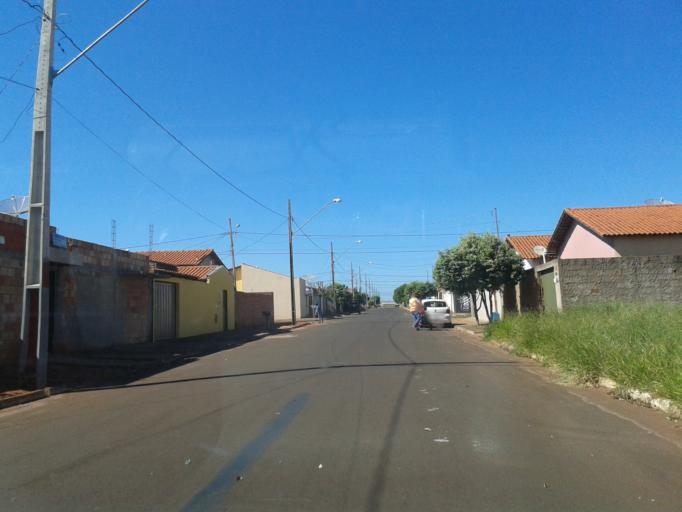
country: BR
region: Minas Gerais
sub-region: Santa Vitoria
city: Santa Vitoria
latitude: -18.8579
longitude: -50.1278
